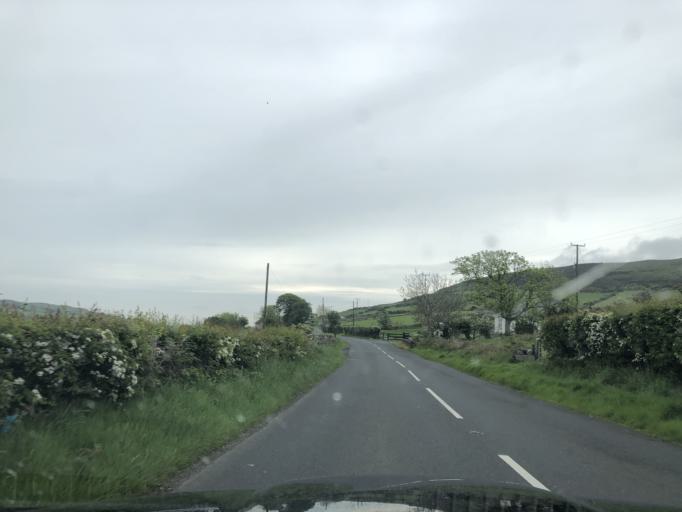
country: GB
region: Northern Ireland
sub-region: Down District
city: Castlewellan
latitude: 54.2195
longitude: -6.0215
